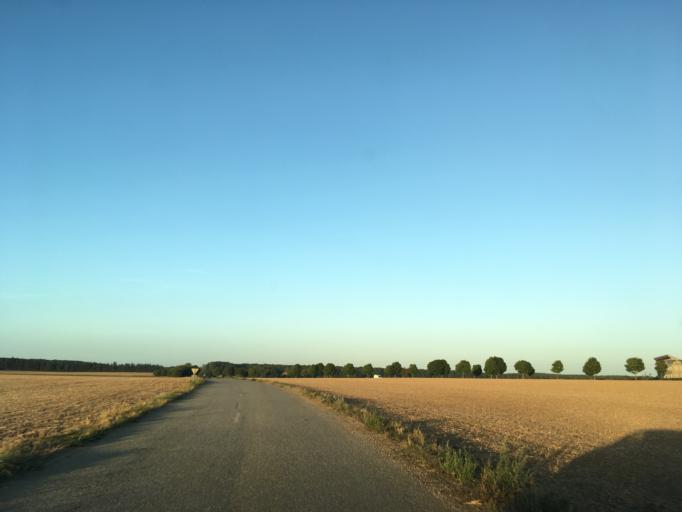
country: FR
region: Haute-Normandie
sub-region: Departement de l'Eure
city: Saint-Marcel
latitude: 49.0675
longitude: 1.4209
